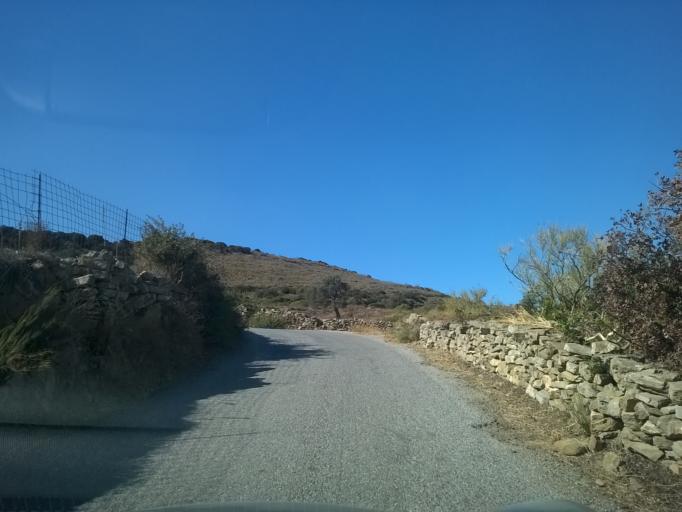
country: GR
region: South Aegean
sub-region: Nomos Kykladon
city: Filotion
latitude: 37.0284
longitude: 25.4264
